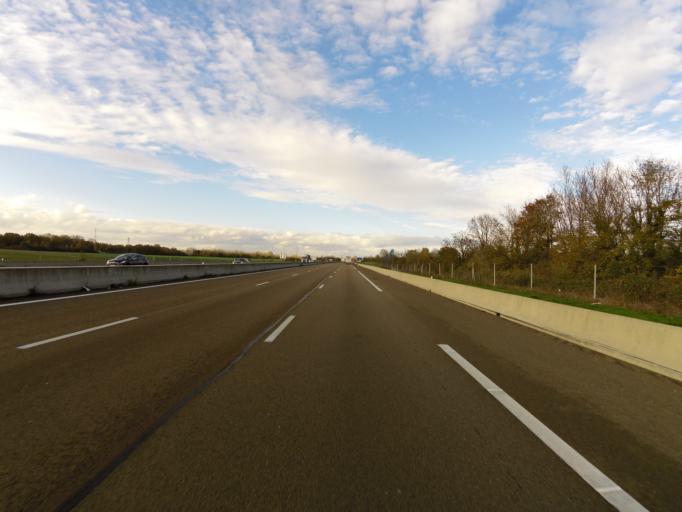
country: FR
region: Bourgogne
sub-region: Departement de la Cote-d'Or
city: Couternon
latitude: 47.3349
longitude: 5.1673
